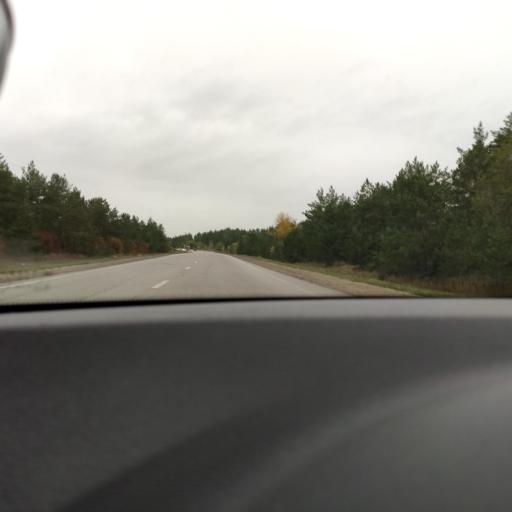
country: RU
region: Samara
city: Mirnyy
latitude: 53.5345
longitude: 50.3028
